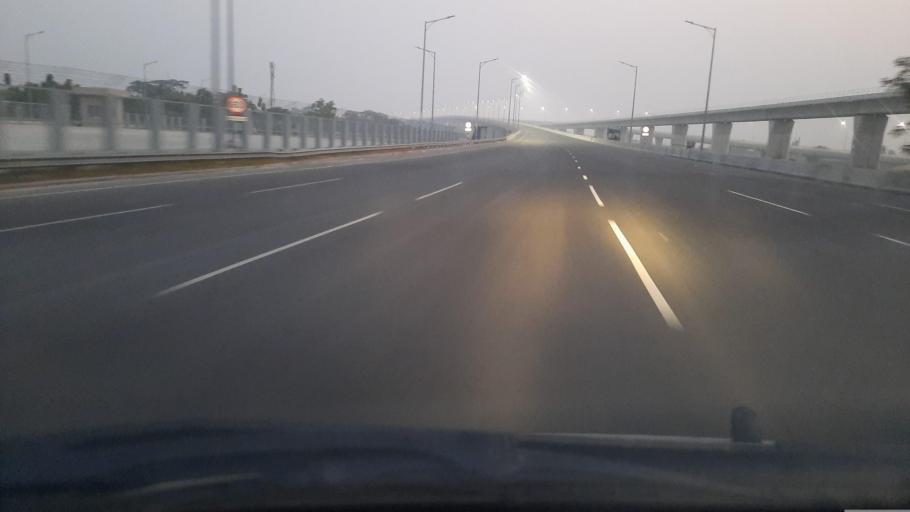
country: BD
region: Dhaka
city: Char Bhadrasan
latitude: 23.4078
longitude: 90.2542
